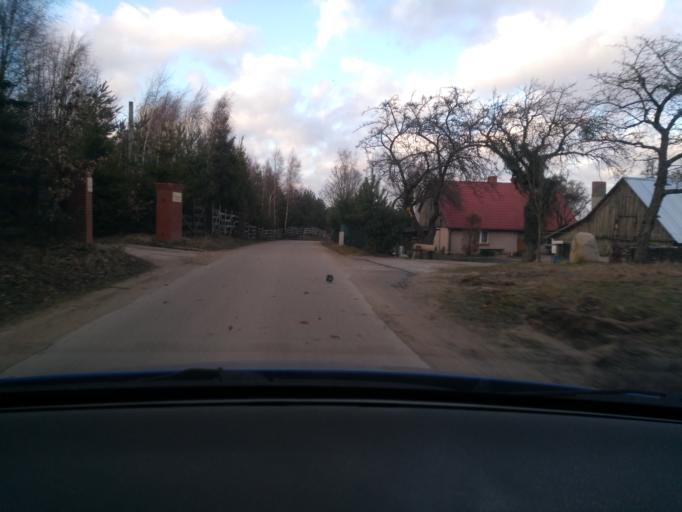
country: PL
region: Pomeranian Voivodeship
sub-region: Powiat kartuski
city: Przodkowo
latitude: 54.4107
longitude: 18.2328
